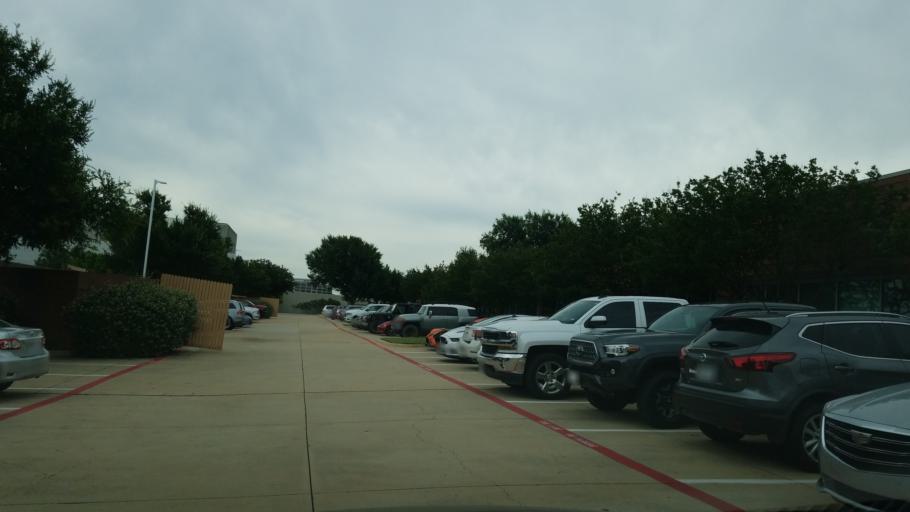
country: US
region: Texas
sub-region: Dallas County
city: Coppell
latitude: 32.8960
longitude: -96.9860
